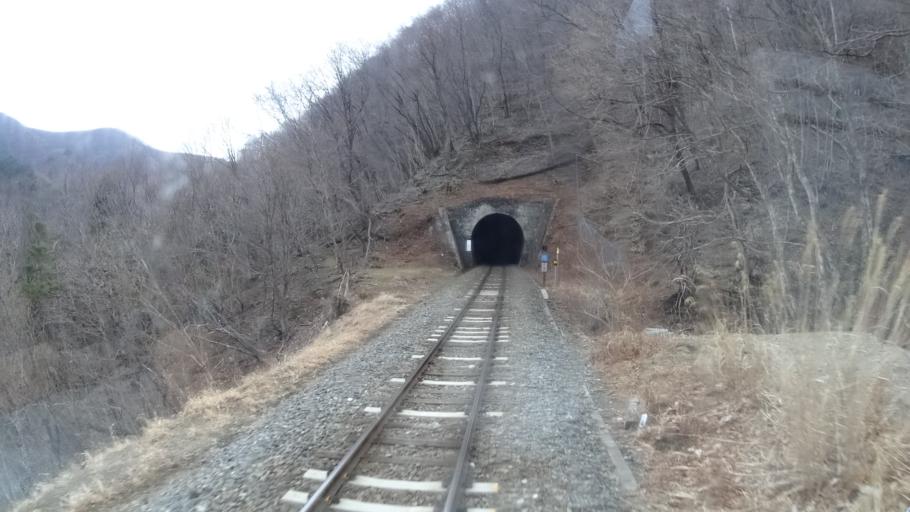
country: JP
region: Iwate
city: Kamaishi
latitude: 39.2746
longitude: 141.7208
